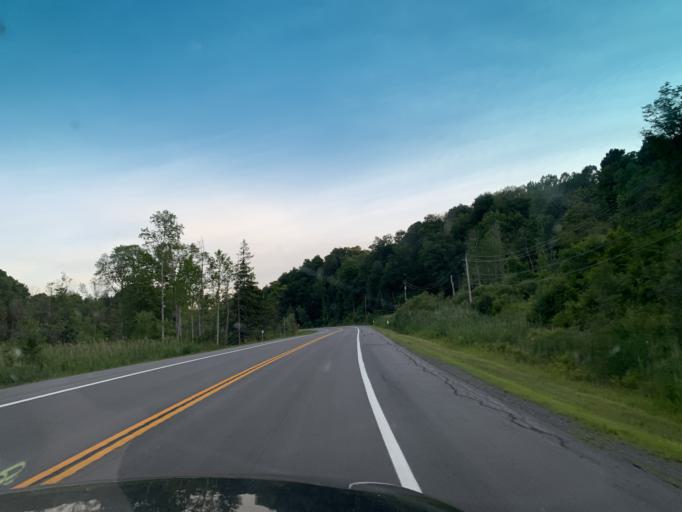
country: US
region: New York
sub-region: Oneida County
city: Chadwicks
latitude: 42.9517
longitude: -75.2423
